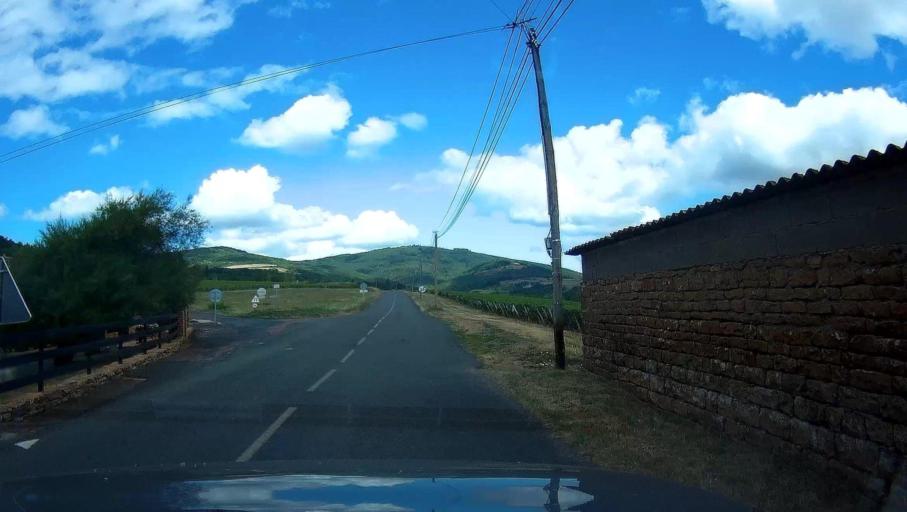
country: FR
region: Rhone-Alpes
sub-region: Departement du Rhone
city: Cogny
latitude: 45.9753
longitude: 4.6063
